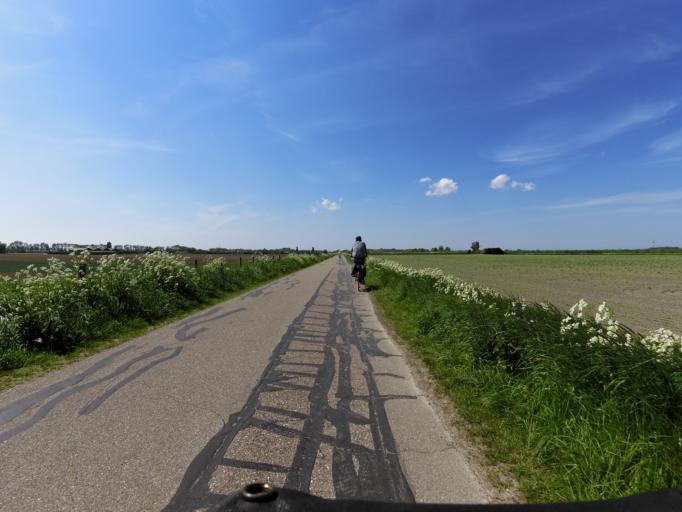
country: NL
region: South Holland
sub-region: Gemeente Binnenmaas
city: Heinenoord
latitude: 51.8272
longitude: 4.5018
